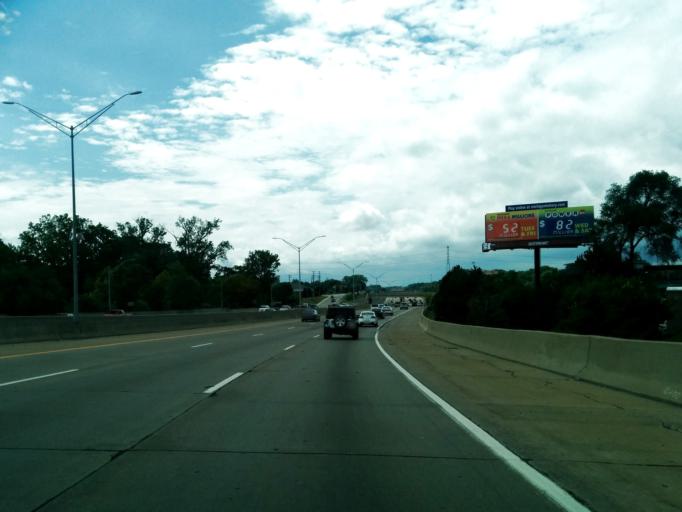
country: US
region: Michigan
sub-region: Macomb County
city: Utica
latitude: 42.6252
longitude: -83.0357
